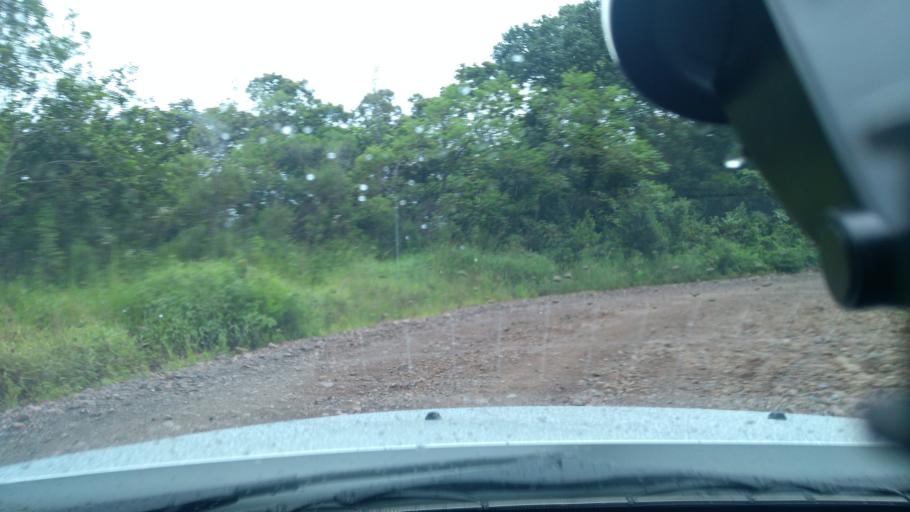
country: BR
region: Rio Grande do Sul
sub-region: Torres
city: Torres
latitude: -29.1905
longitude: -49.9830
